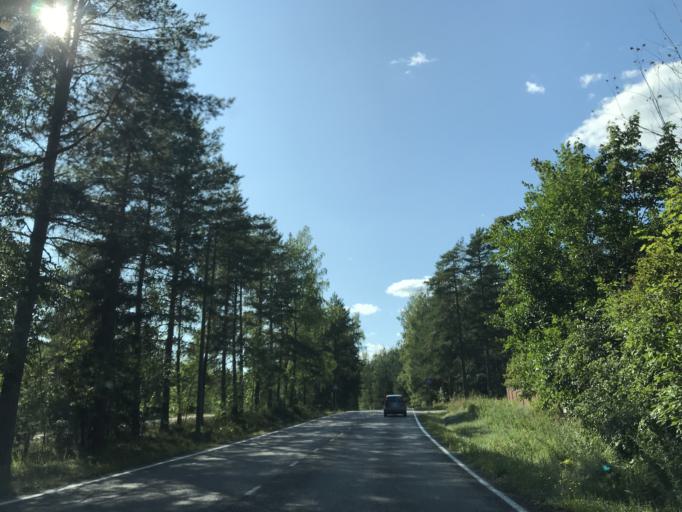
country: FI
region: Uusimaa
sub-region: Helsinki
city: Tuusula
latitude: 60.4047
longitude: 24.9856
